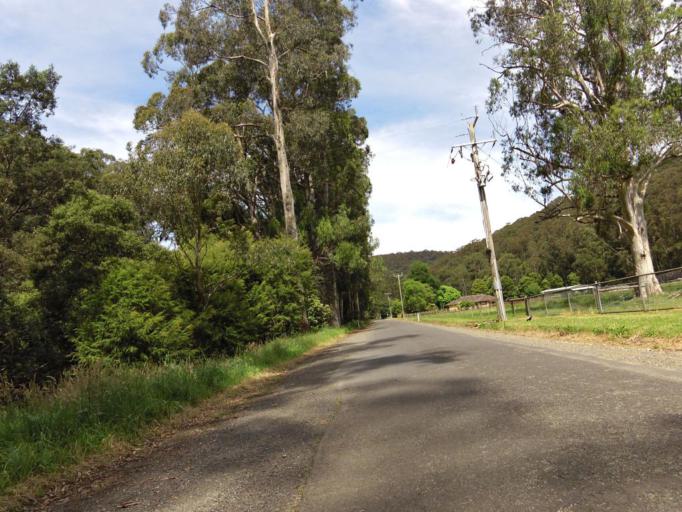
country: AU
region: Victoria
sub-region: Yarra Ranges
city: Millgrove
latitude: -37.7506
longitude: 145.7192
